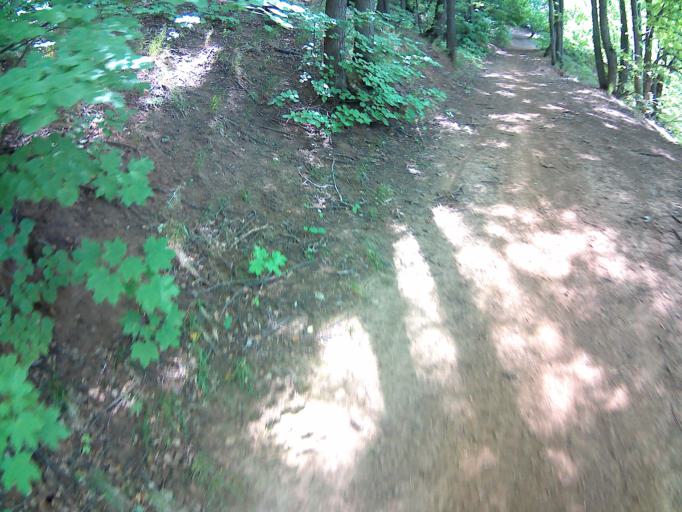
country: RU
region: Nizjnij Novgorod
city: Nizhniy Novgorod
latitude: 56.2396
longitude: 43.9392
